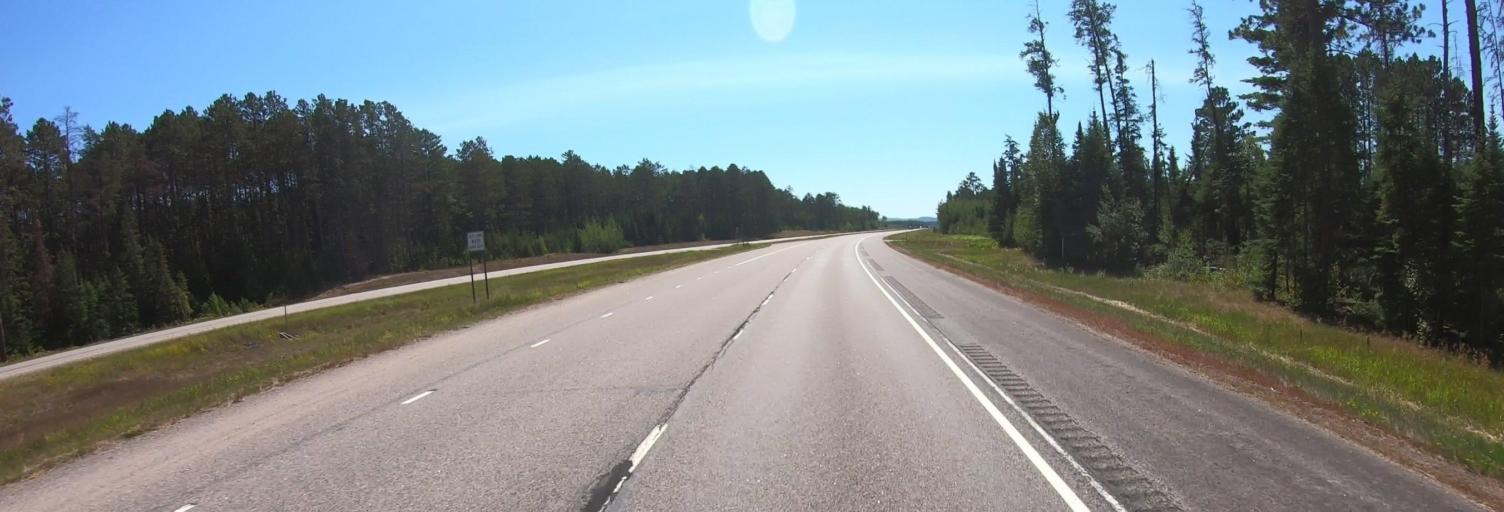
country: US
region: Minnesota
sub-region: Saint Louis County
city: Parkville
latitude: 47.6555
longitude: -92.5732
